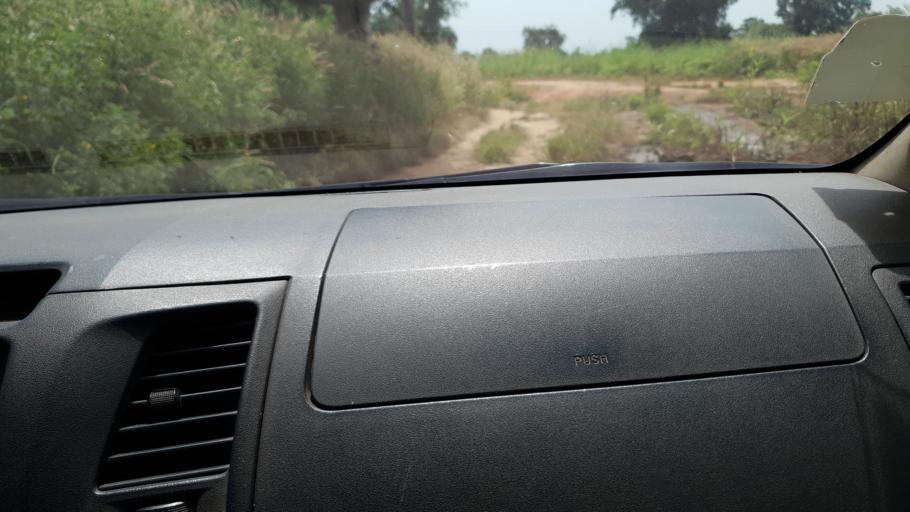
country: ML
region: Koulikoro
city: Kolokani
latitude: 13.4275
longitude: -8.2418
